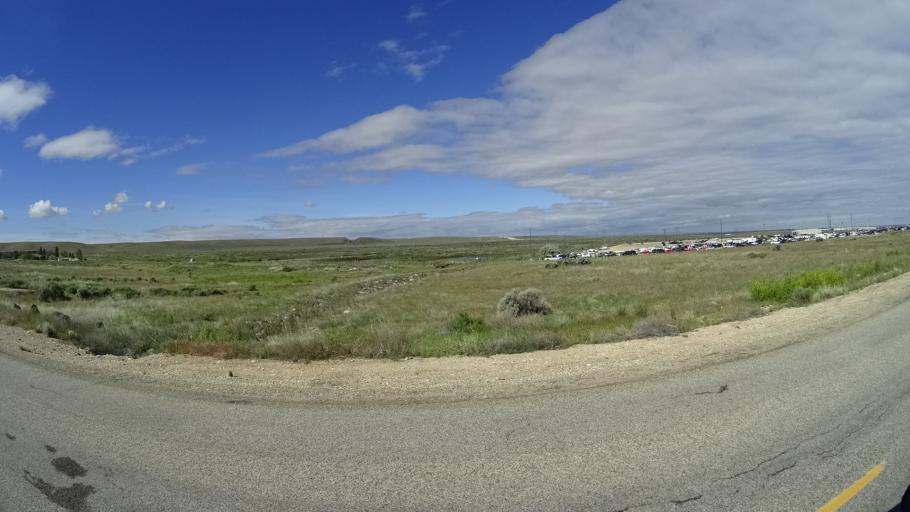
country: US
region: Idaho
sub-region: Ada County
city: Boise
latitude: 43.5318
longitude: -116.1583
